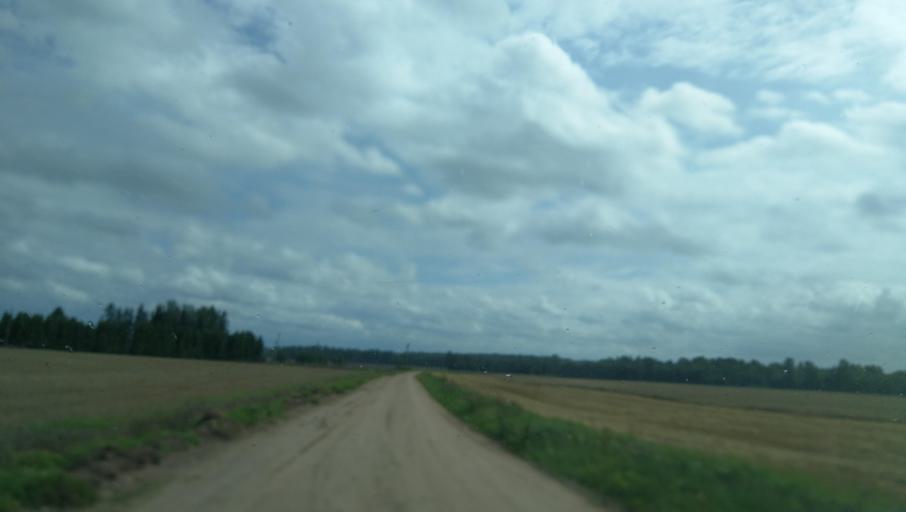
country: LV
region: Beverina
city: Murmuiza
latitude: 57.4060
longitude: 25.4526
